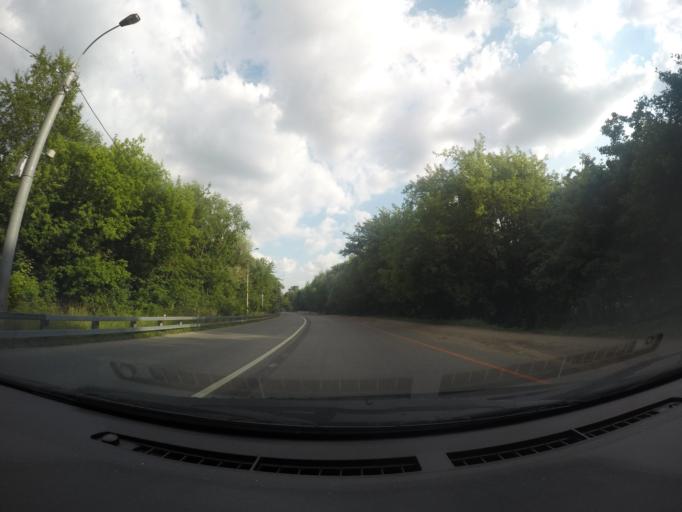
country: RU
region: Moscow
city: Sviblovo
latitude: 55.8446
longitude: 37.6268
